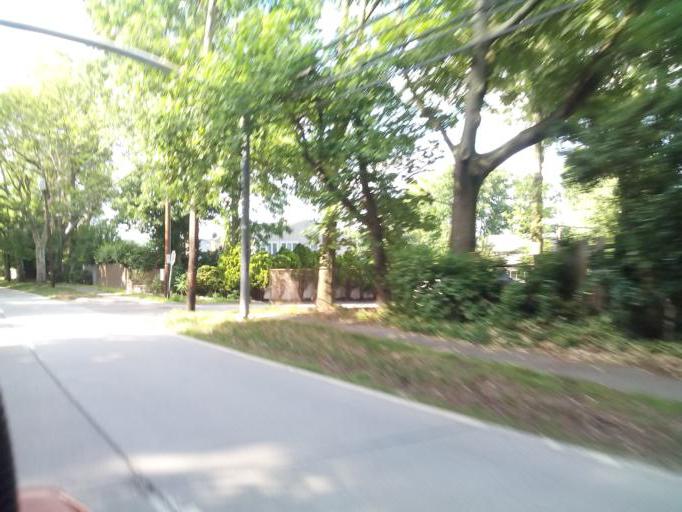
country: US
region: New York
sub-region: Nassau County
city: Lattingtown
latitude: 40.9022
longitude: -73.5839
